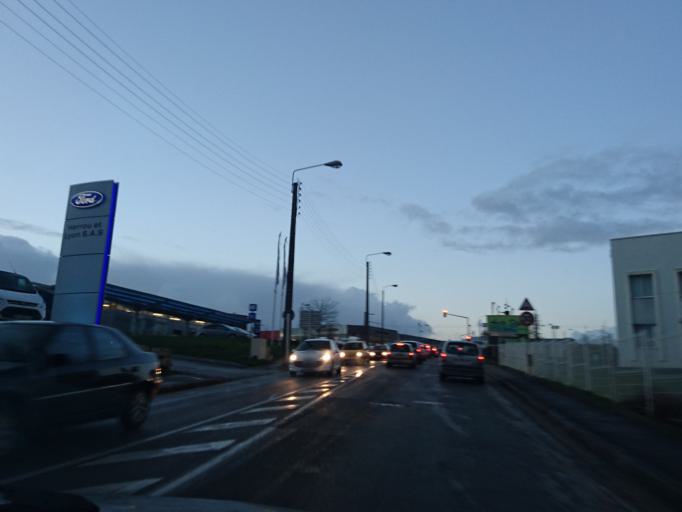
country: FR
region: Brittany
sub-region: Departement du Finistere
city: Brest
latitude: 48.4157
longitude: -4.4620
